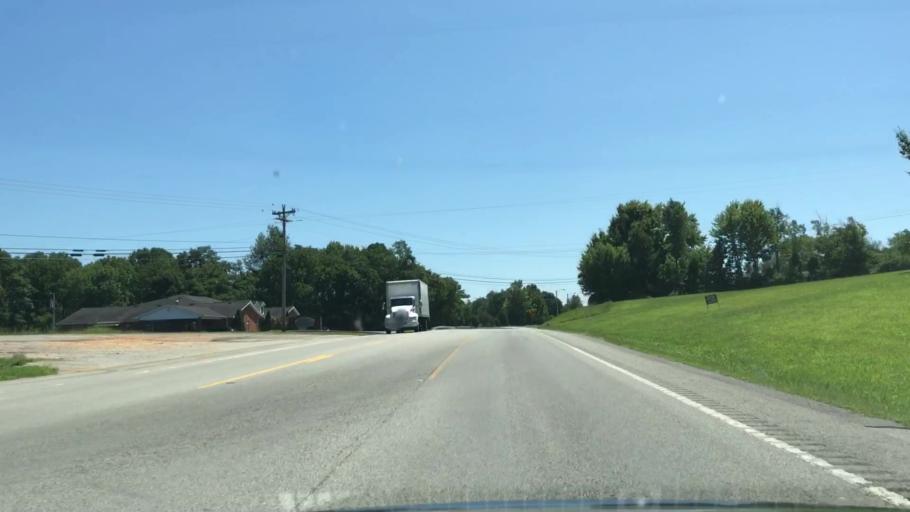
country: US
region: Tennessee
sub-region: Jackson County
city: Gainesboro
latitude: 36.3035
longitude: -85.6407
